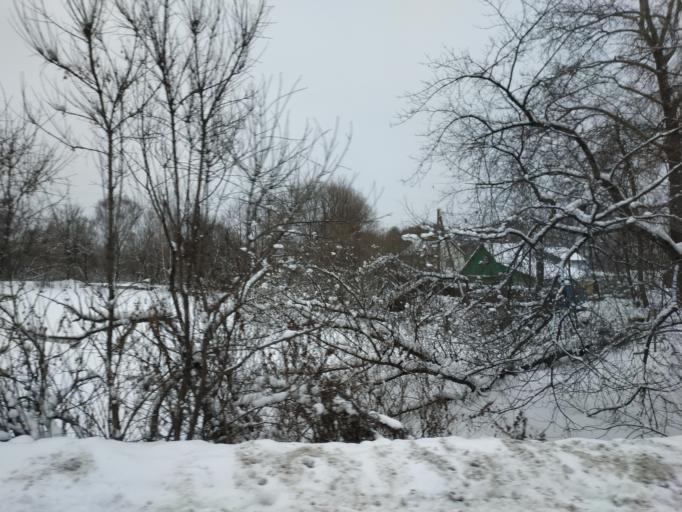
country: RU
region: Moskovskaya
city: Balashikha
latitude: 55.8349
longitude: 37.9454
